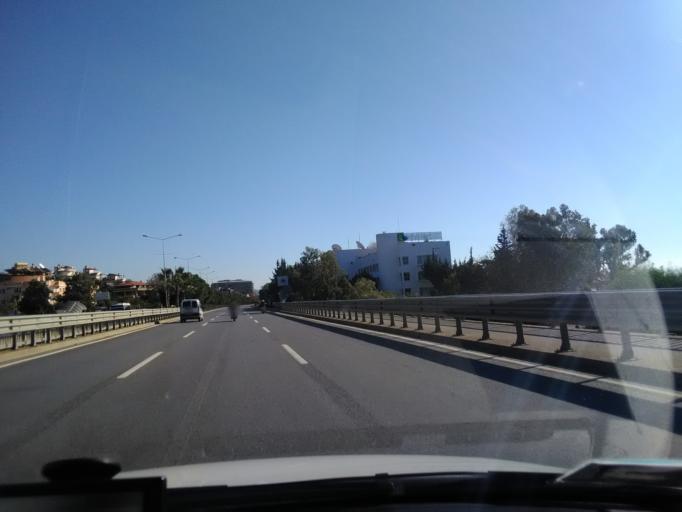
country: TR
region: Antalya
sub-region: Alanya
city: Mahmutlar
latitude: 36.5227
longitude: 32.0543
